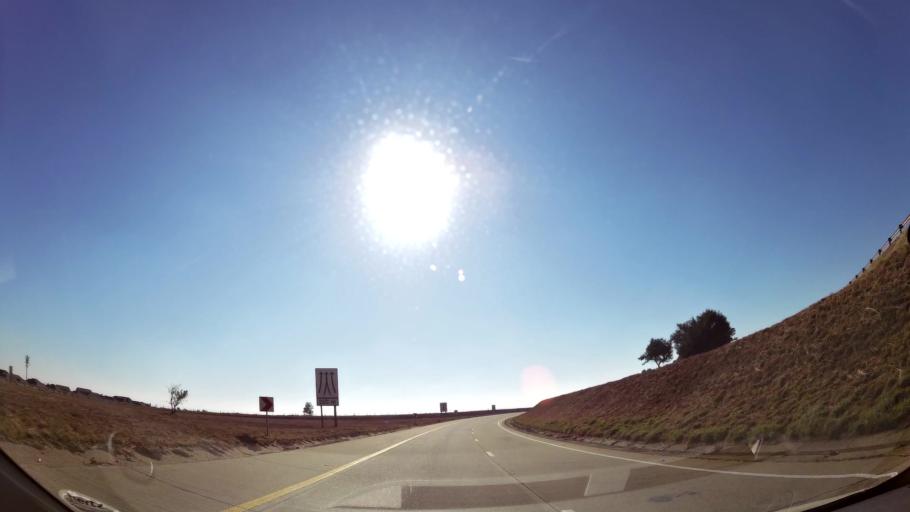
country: ZA
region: Mpumalanga
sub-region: Nkangala District Municipality
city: Witbank
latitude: -25.8962
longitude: 29.2548
